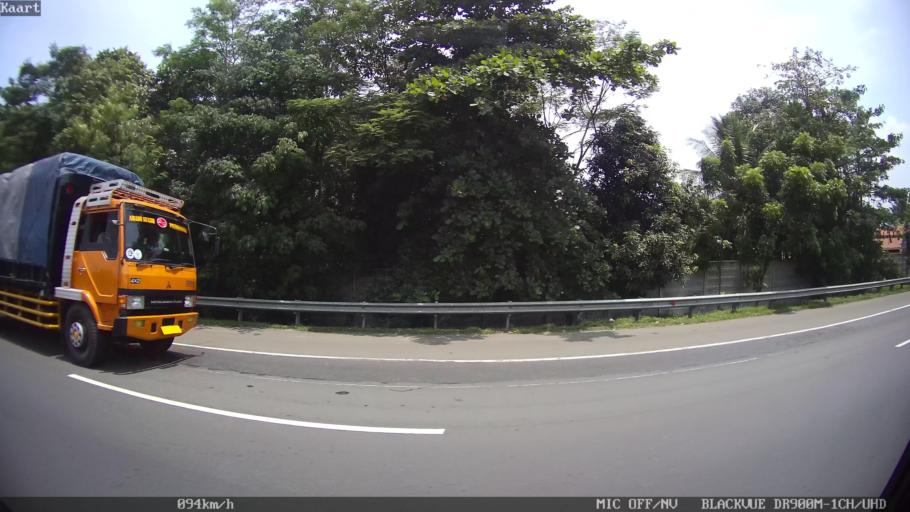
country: ID
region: West Java
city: Kresek
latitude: -6.1792
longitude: 106.3898
